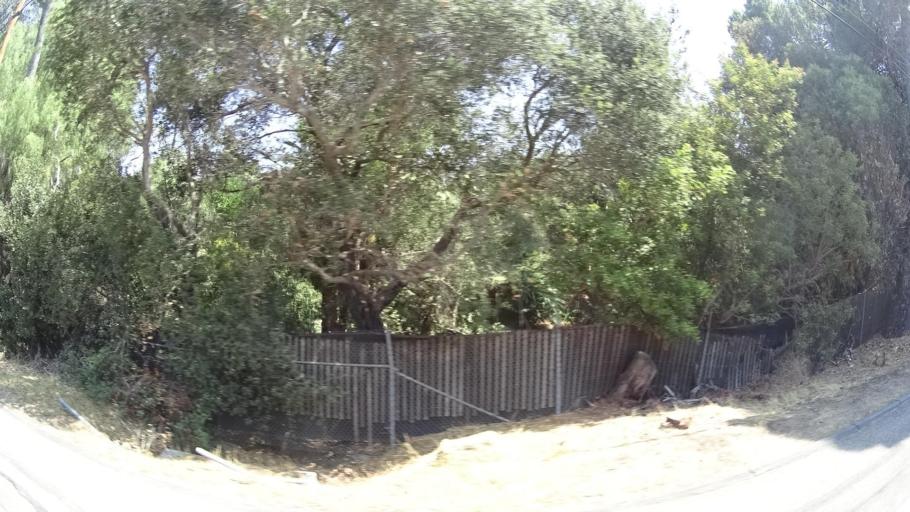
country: US
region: California
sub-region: San Diego County
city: Bonsall
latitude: 33.2550
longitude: -117.2343
